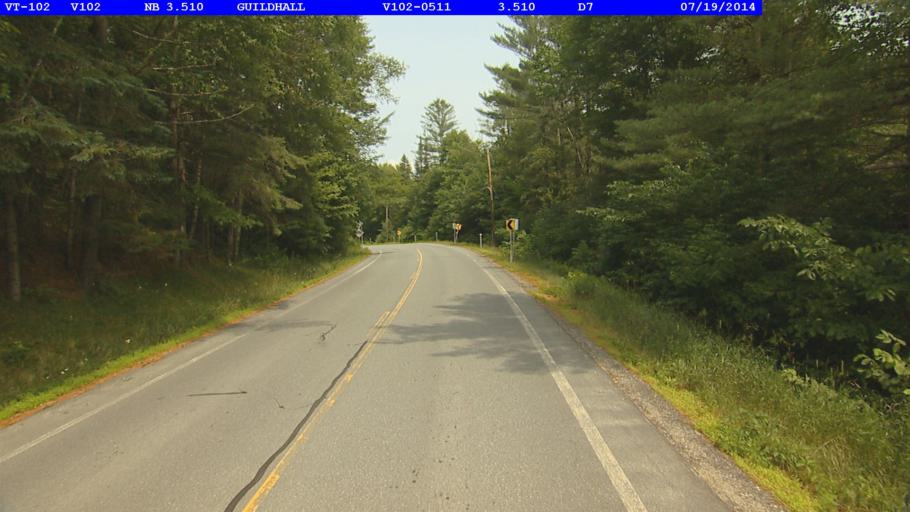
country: US
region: New Hampshire
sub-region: Coos County
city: Northumberland
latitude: 44.5434
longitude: -71.5829
